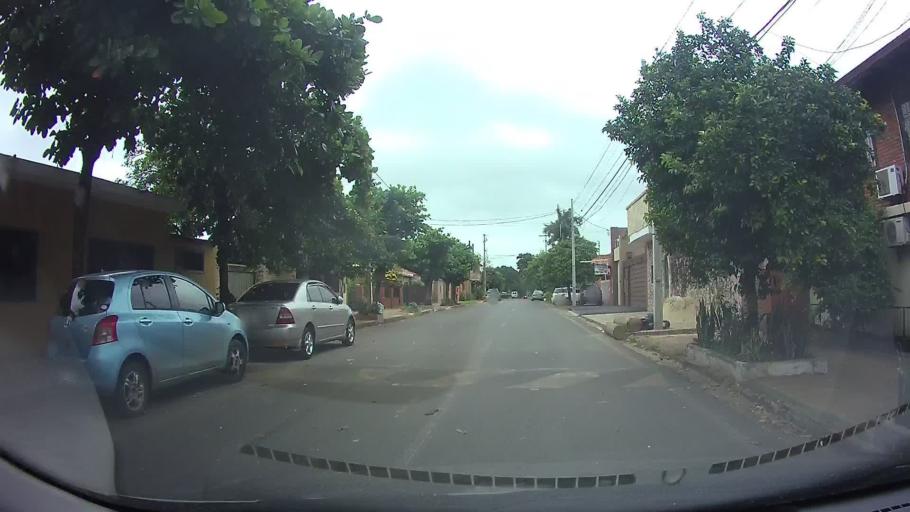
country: PY
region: Central
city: San Lorenzo
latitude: -25.2690
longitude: -57.4971
